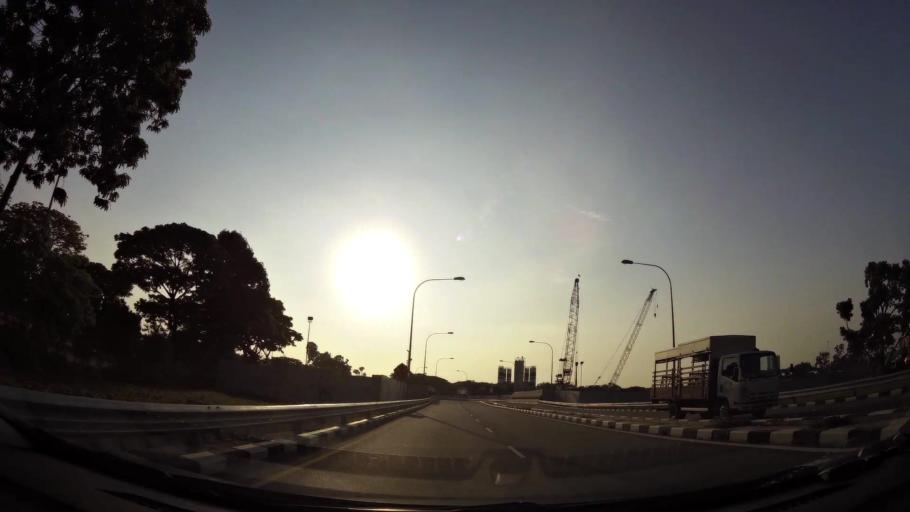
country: SG
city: Singapore
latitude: 1.2802
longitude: 103.8678
